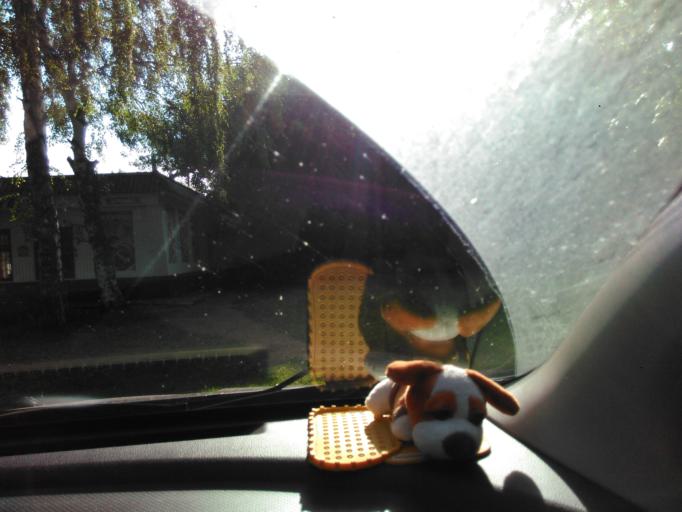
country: RU
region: Penza
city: Lermontovo
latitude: 52.9938
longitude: 43.6583
